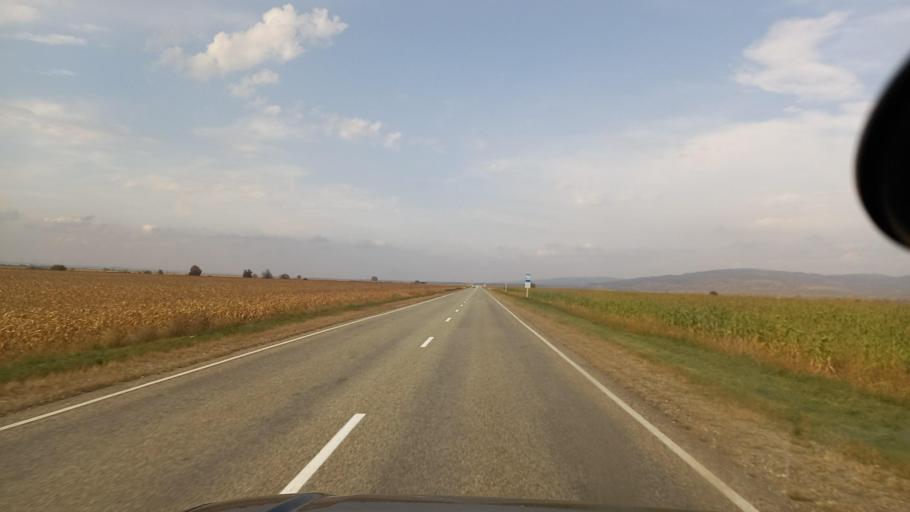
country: RU
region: Krasnodarskiy
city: Shedok
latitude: 44.2771
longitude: 40.8681
